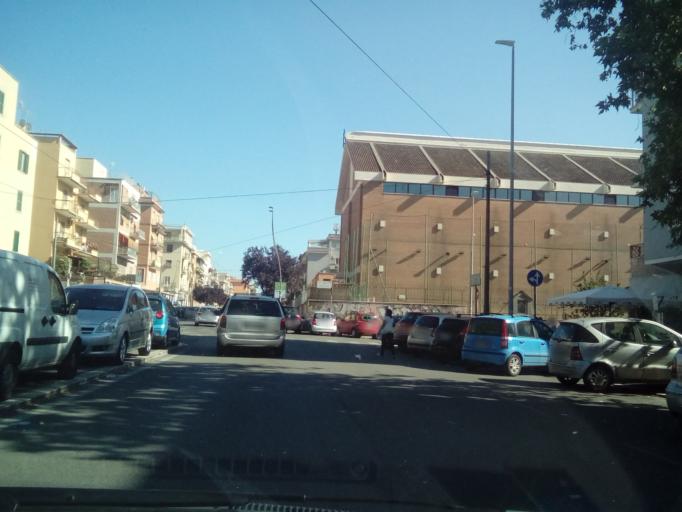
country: IT
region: Latium
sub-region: Citta metropolitana di Roma Capitale
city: Rome
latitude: 41.8905
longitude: 12.5645
